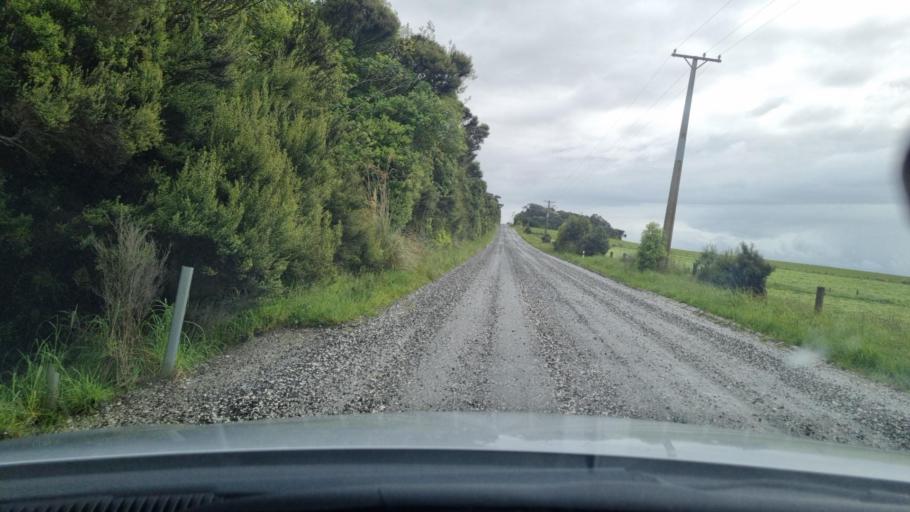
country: NZ
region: Southland
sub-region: Invercargill City
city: Bluff
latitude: -46.5315
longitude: 168.2678
